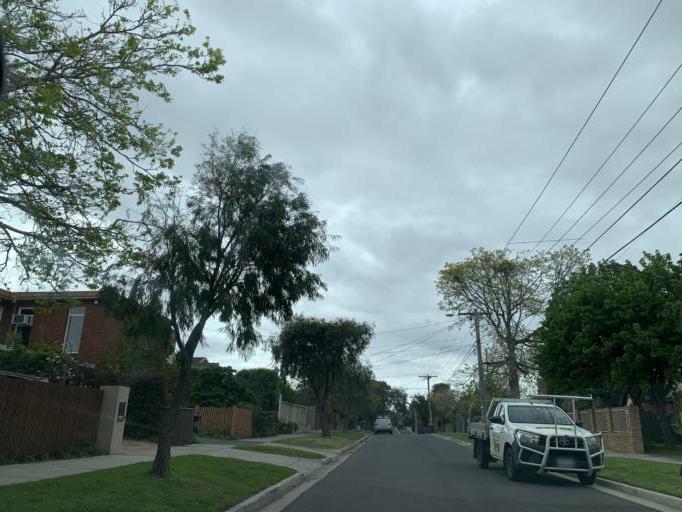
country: AU
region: Victoria
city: Beaumaris
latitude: -37.9889
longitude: 145.0406
